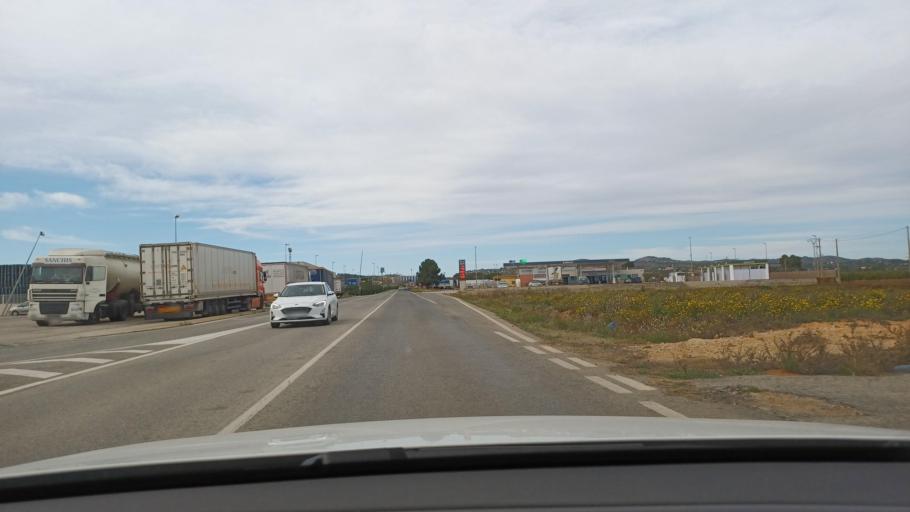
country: ES
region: Valencia
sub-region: Provincia de Valencia
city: Benifaio
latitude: 39.2882
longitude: -0.4477
